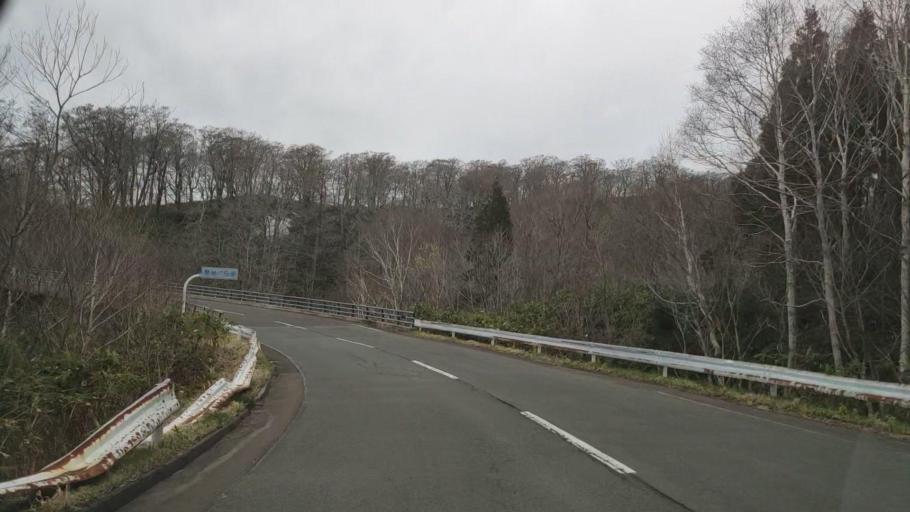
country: JP
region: Akita
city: Hanawa
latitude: 40.4177
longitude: 140.8404
